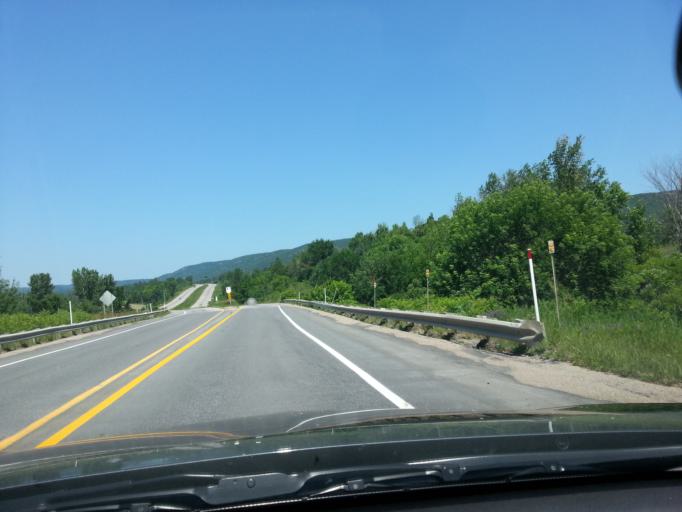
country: CA
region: Quebec
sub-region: Outaouais
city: Wakefield
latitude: 45.5075
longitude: -75.9730
